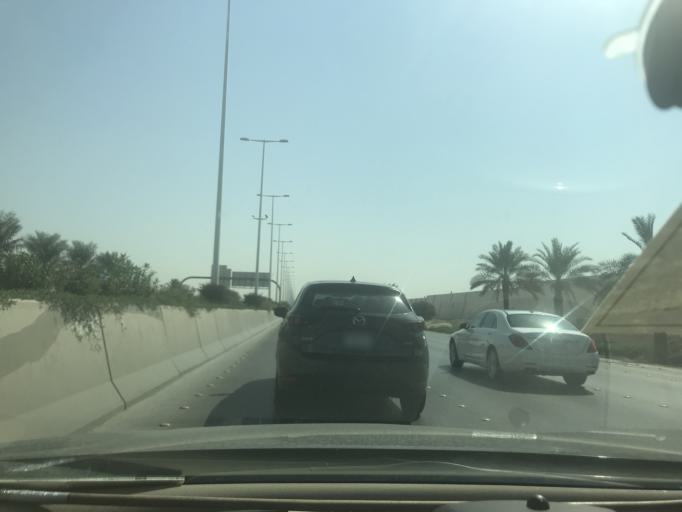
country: SA
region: Ar Riyad
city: Riyadh
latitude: 24.7211
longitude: 46.7127
